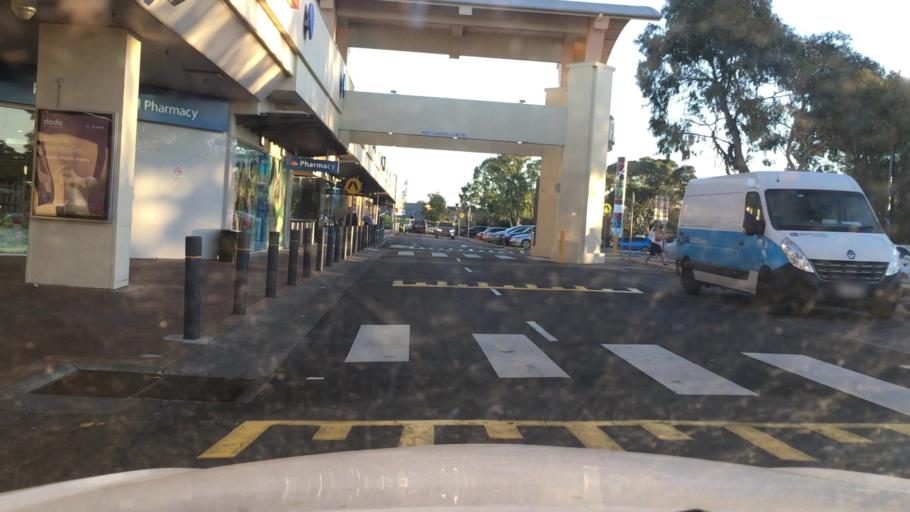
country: AU
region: Victoria
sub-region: Greater Dandenong
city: Keysborough
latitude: -37.9925
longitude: 145.1716
